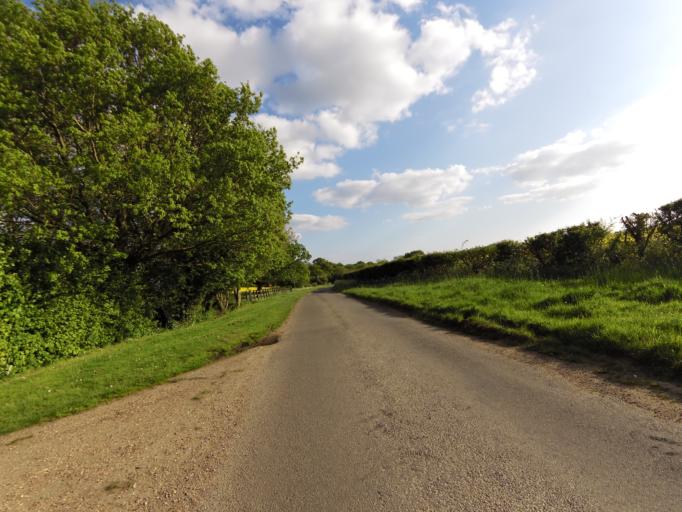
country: GB
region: England
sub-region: Suffolk
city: Halesworth
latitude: 52.4104
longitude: 1.5073
